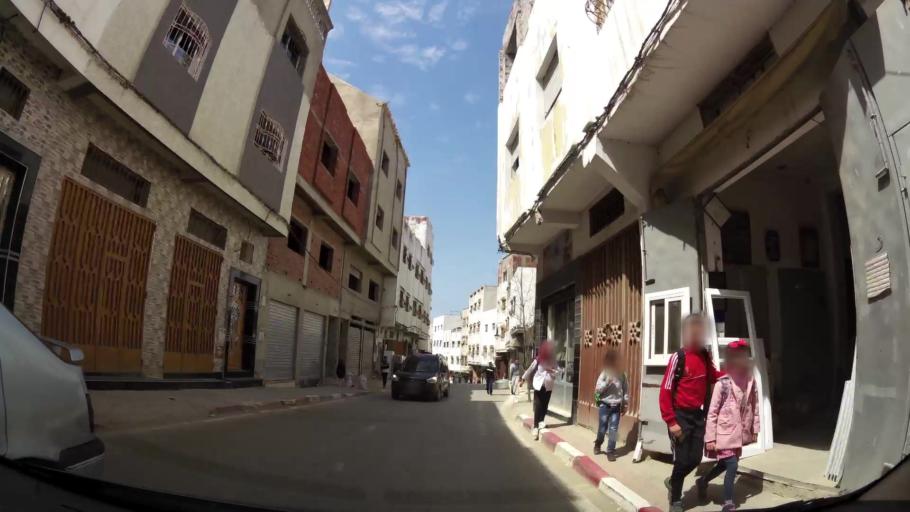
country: MA
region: Tanger-Tetouan
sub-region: Tanger-Assilah
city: Tangier
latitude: 35.7404
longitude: -5.8271
